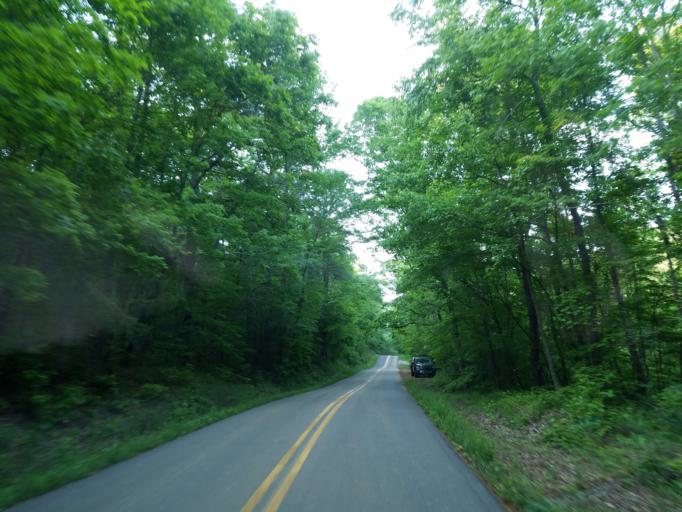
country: US
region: Georgia
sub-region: Gordon County
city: Calhoun
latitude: 34.5717
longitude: -85.1003
